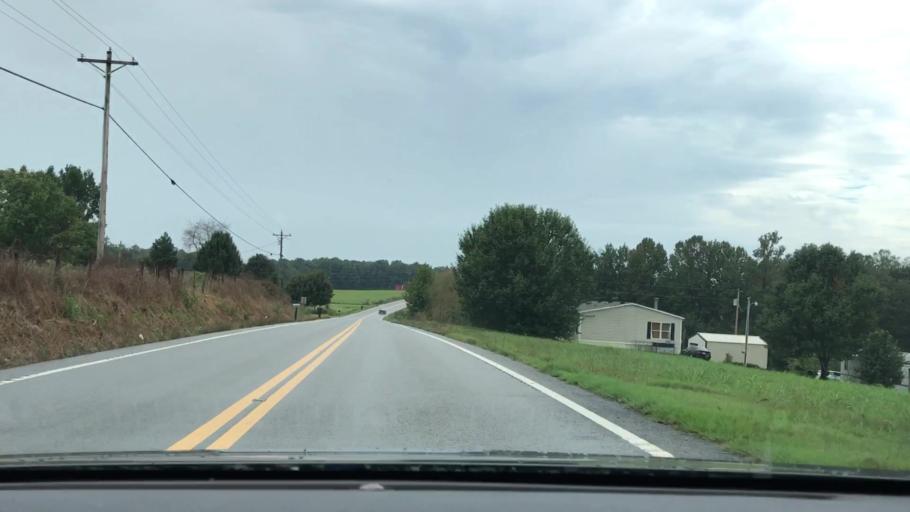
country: US
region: Tennessee
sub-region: Macon County
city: Red Boiling Springs
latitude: 36.5582
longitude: -85.8025
